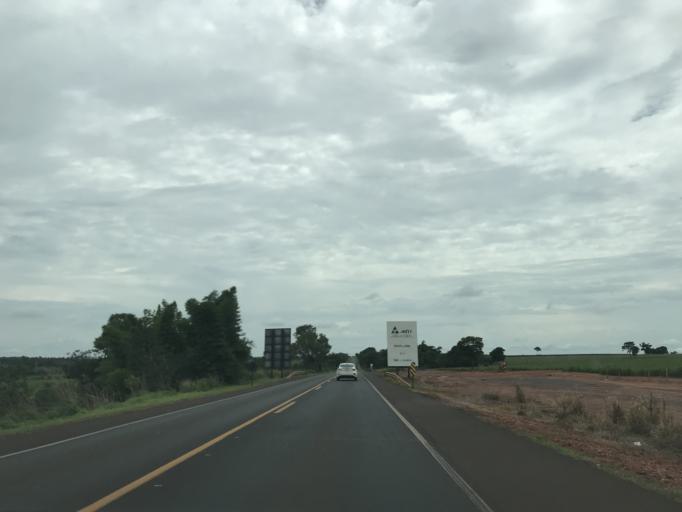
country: BR
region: Minas Gerais
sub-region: Frutal
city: Frutal
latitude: -20.0636
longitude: -49.0648
